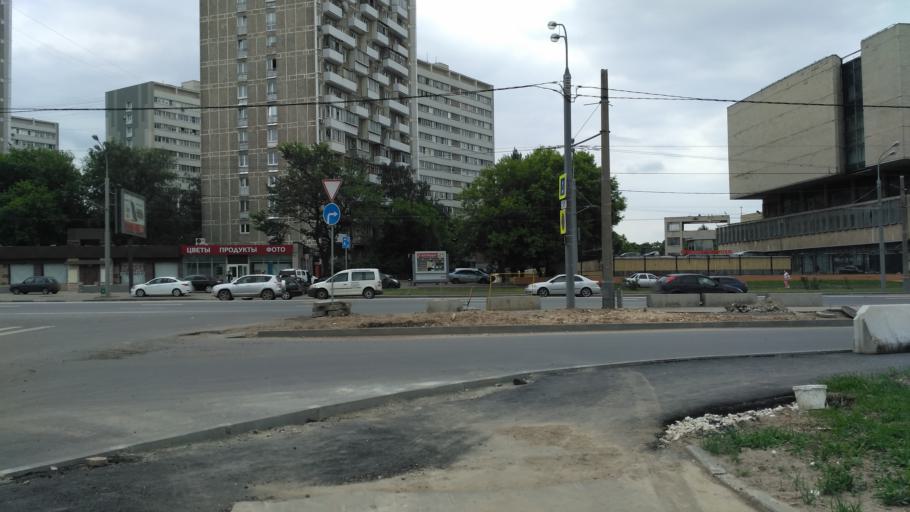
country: RU
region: Moscow
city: Metrogorodok
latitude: 55.8045
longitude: 37.7588
